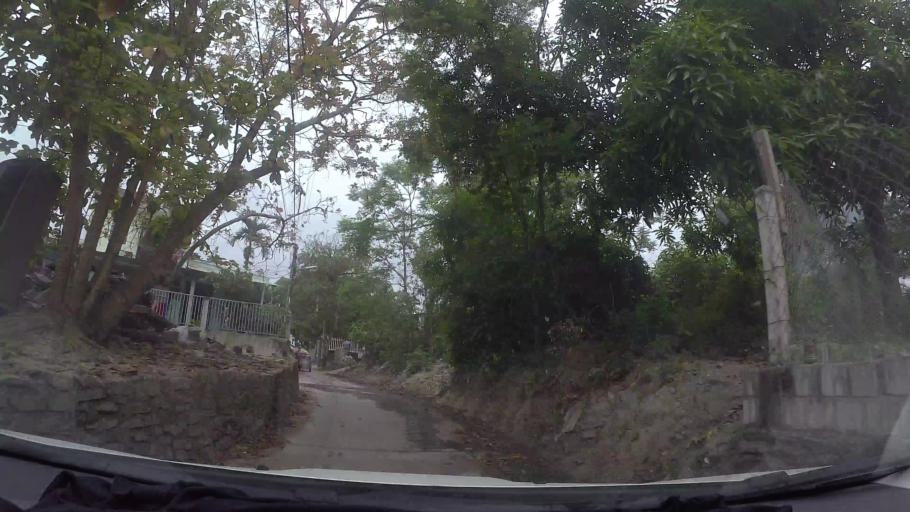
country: VN
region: Da Nang
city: Lien Chieu
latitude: 16.0772
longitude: 108.0968
